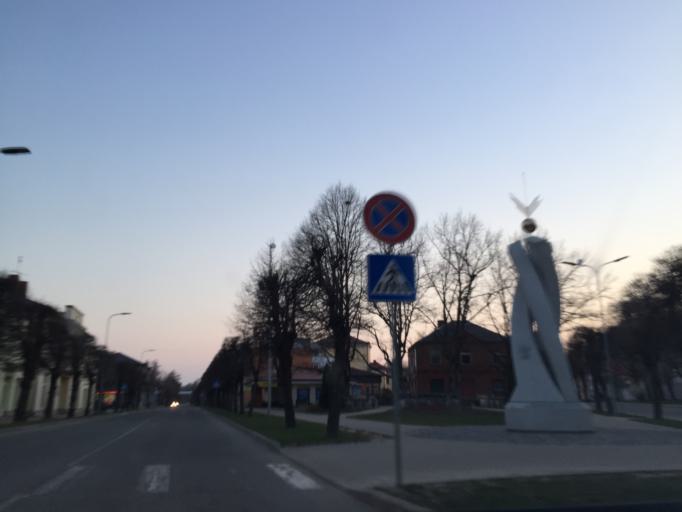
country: LV
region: Valkas Rajons
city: Valka
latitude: 57.7751
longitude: 26.0209
